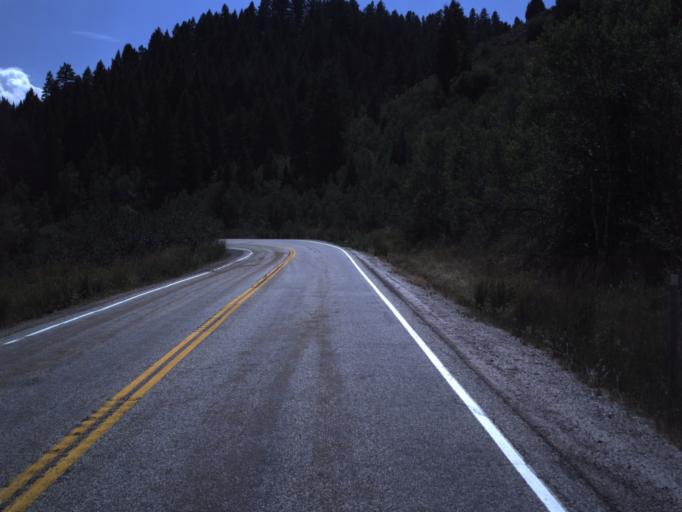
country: US
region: Utah
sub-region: Cache County
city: North Logan
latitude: 41.8537
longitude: -111.5863
